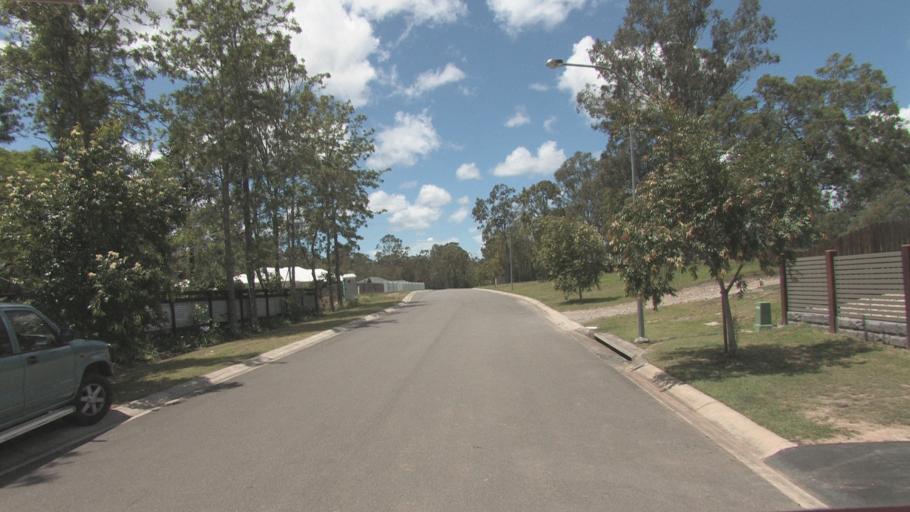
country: AU
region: Queensland
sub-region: Logan
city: Beenleigh
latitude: -27.6659
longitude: 153.2189
